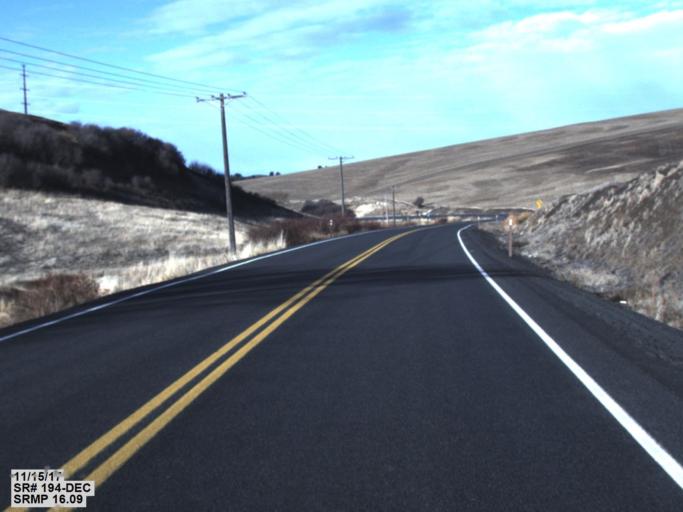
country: US
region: Washington
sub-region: Whitman County
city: Pullman
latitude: 46.7291
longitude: -117.3006
